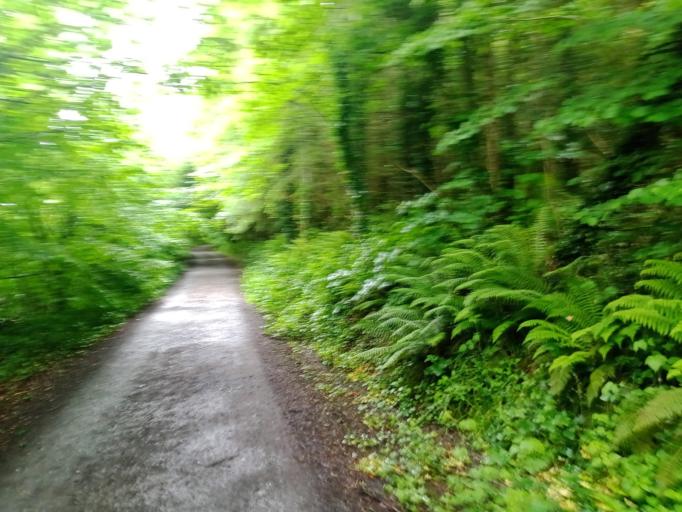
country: IE
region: Leinster
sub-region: Kilkenny
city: Thomastown
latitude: 52.4817
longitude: -7.0487
